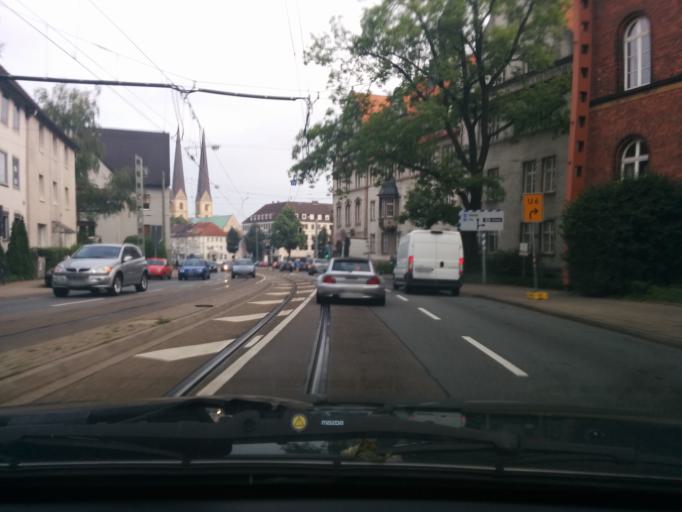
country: DE
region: North Rhine-Westphalia
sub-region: Regierungsbezirk Detmold
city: Bielefeld
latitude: 52.0149
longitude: 8.5330
